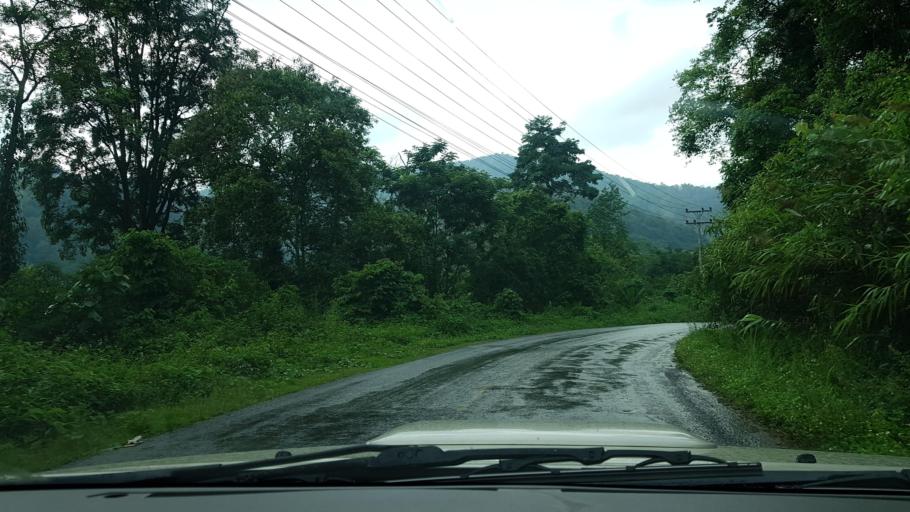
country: LA
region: Oudomxai
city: Muang Xay
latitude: 20.6002
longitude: 101.9416
